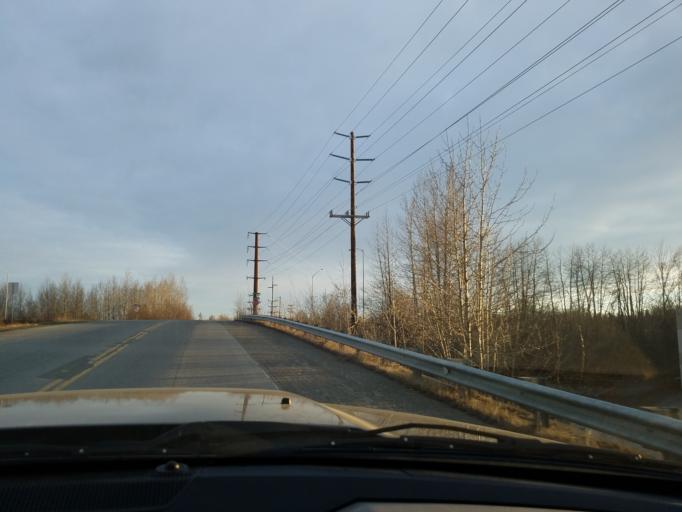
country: US
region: Alaska
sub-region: Anchorage Municipality
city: Anchorage
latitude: 61.1719
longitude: -149.9129
